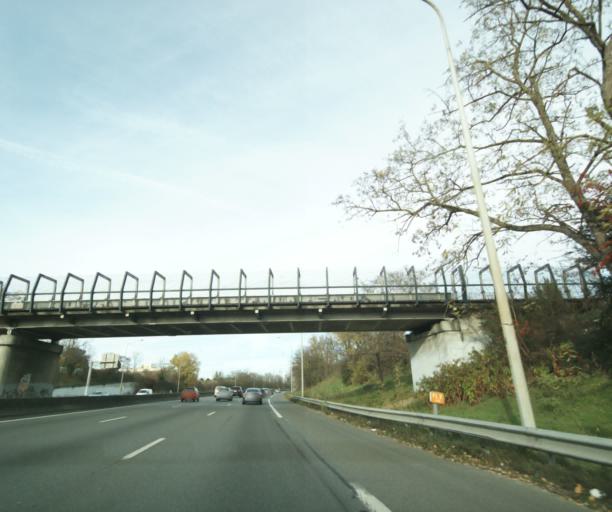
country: FR
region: Midi-Pyrenees
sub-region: Departement de la Haute-Garonne
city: Blagnac
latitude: 43.5960
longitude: 1.3973
